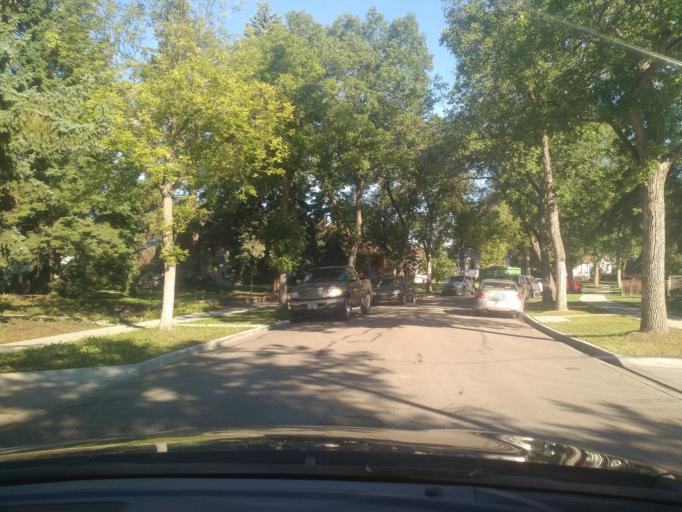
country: CA
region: Alberta
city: Edmonton
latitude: 53.4993
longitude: -113.5211
